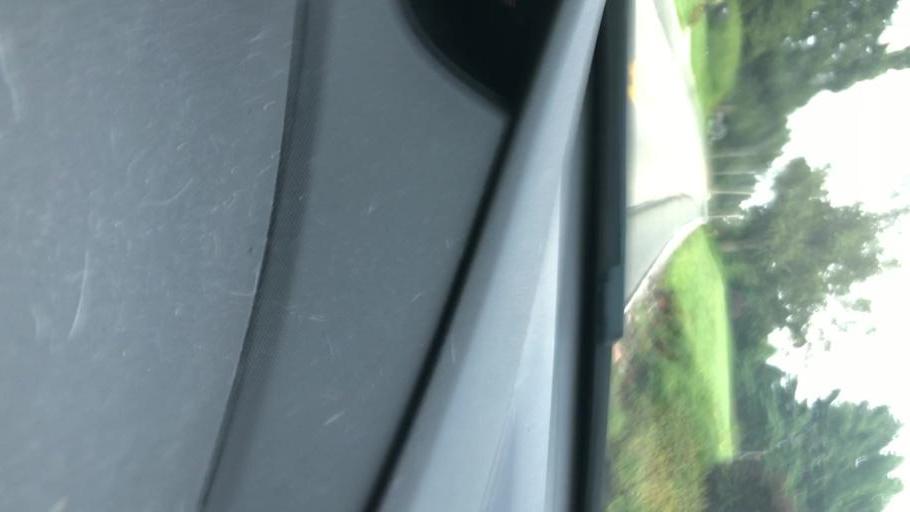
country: US
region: Pennsylvania
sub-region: Montgomery County
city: Limerick
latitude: 40.2078
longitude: -75.5131
